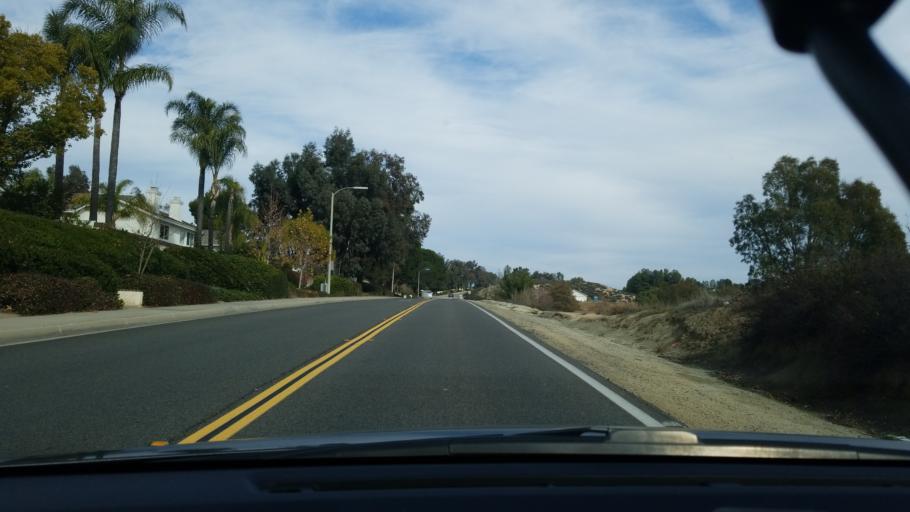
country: US
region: California
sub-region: Riverside County
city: Temecula
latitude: 33.5059
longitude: -117.1090
